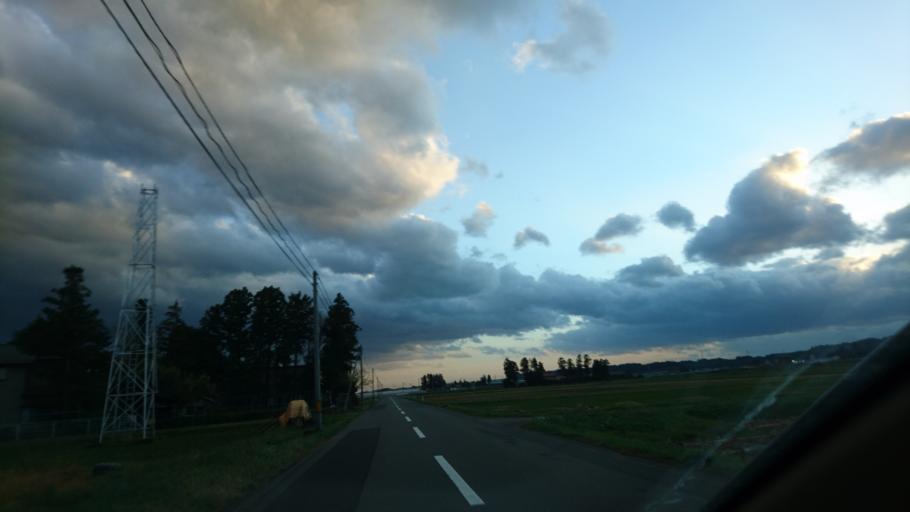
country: JP
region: Iwate
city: Mizusawa
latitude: 39.1097
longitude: 141.1502
